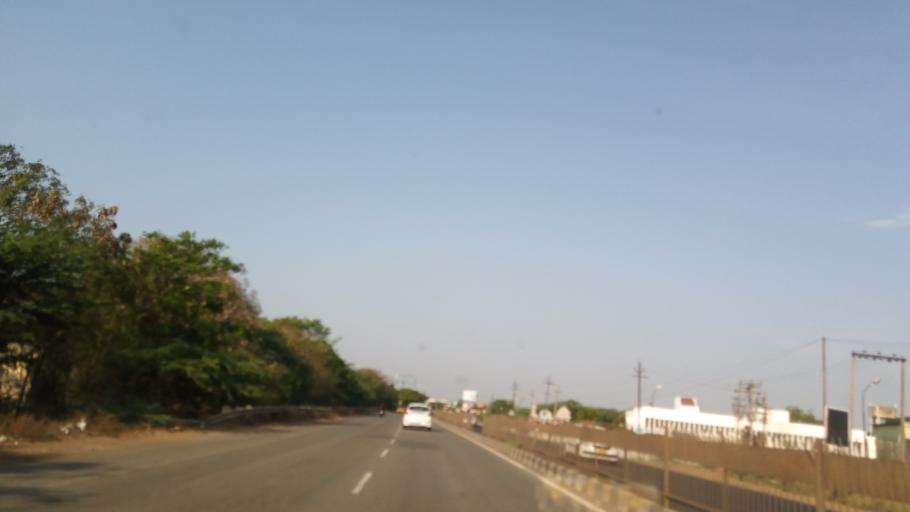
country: IN
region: Tamil Nadu
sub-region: Kancheepuram
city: Poonamalle
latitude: 13.0421
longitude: 80.0606
